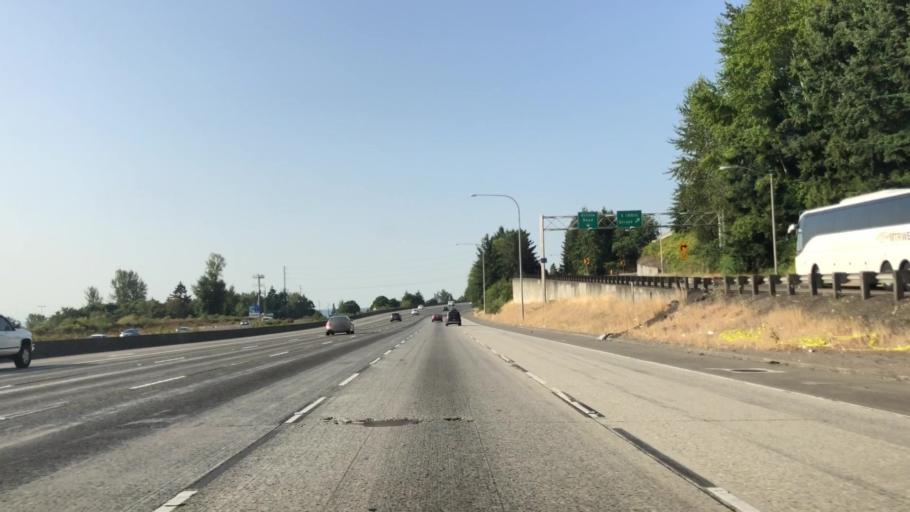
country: US
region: Washington
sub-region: King County
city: SeaTac
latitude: 47.4363
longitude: -122.2699
